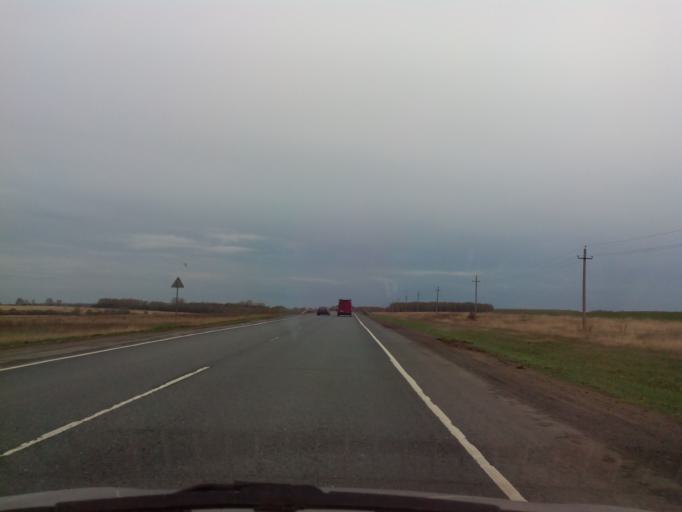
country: RU
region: Moskovskaya
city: Ozherel'ye
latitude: 54.6419
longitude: 38.3696
